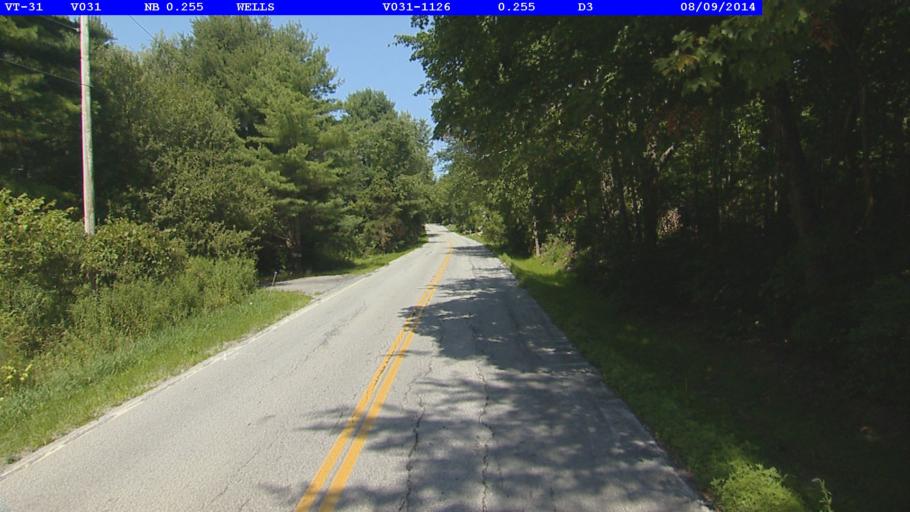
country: US
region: New York
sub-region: Washington County
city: Granville
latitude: 43.4418
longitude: -73.2482
